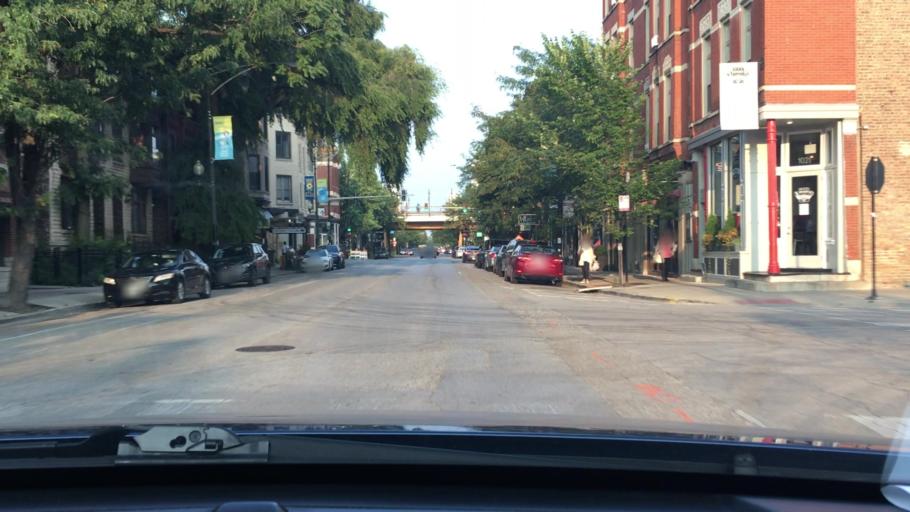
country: US
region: Illinois
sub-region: Cook County
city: Chicago
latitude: 41.9181
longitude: -87.6546
